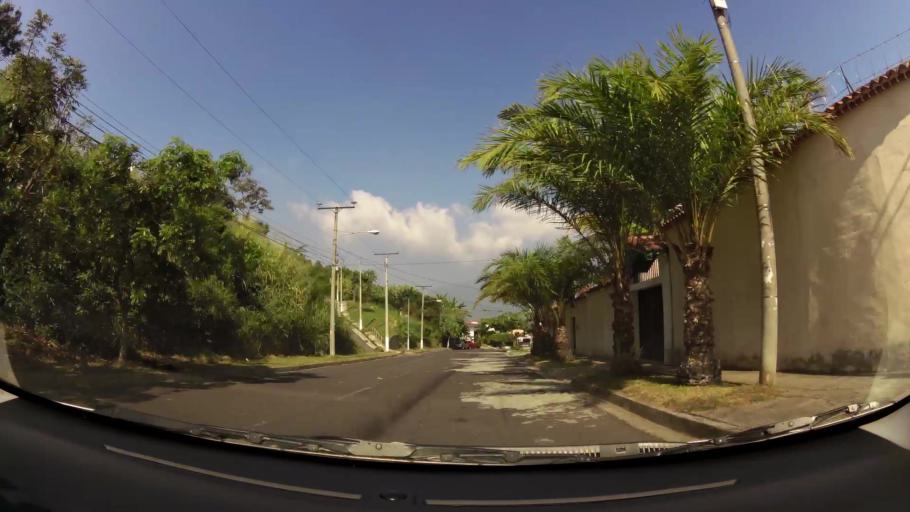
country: SV
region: La Libertad
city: Antiguo Cuscatlan
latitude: 13.6718
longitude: -89.2344
